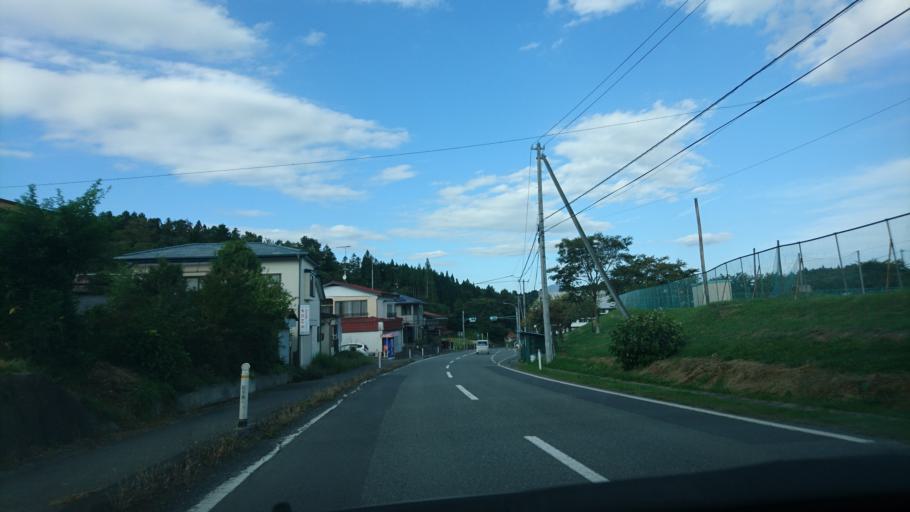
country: JP
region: Iwate
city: Ichinoseki
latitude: 38.8669
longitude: 141.3498
